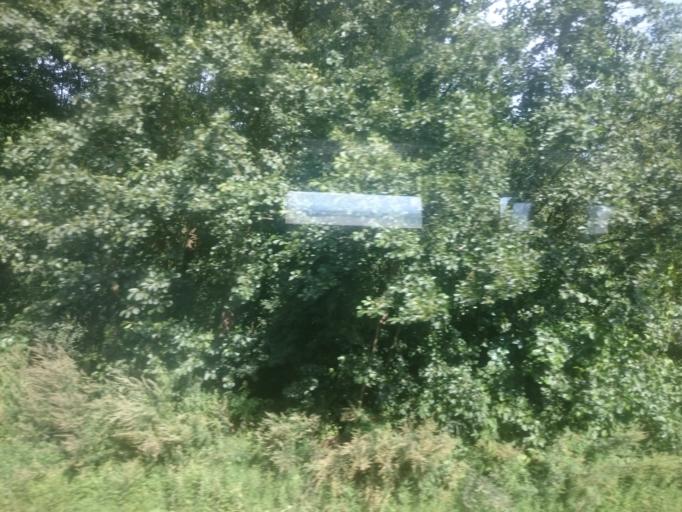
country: RU
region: Kaliningrad
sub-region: Zelenogradskiy Rayon
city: Zelenogradsk
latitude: 54.9443
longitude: 20.4163
